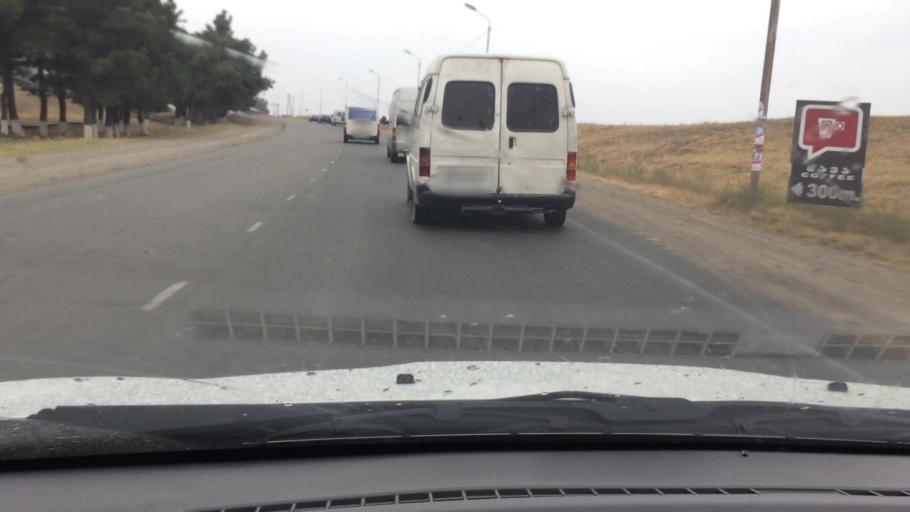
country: GE
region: Kvemo Kartli
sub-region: Marneuli
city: Marneuli
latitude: 41.5031
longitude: 44.8019
